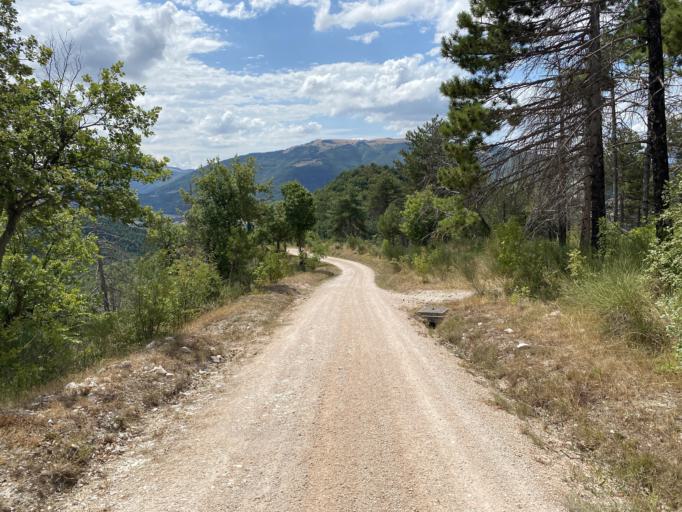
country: IT
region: The Marches
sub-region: Provincia di Pesaro e Urbino
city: Canavaccio
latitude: 43.7072
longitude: 12.7149
